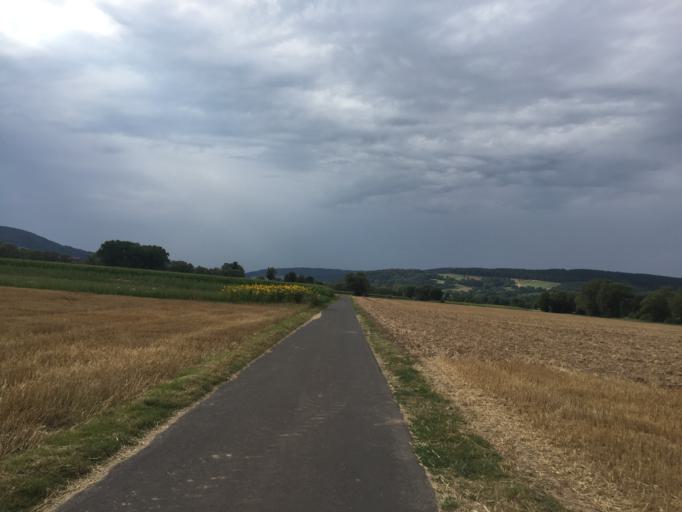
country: DE
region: Hesse
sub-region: Regierungsbezirk Kassel
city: Alheim
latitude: 51.0387
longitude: 9.6663
